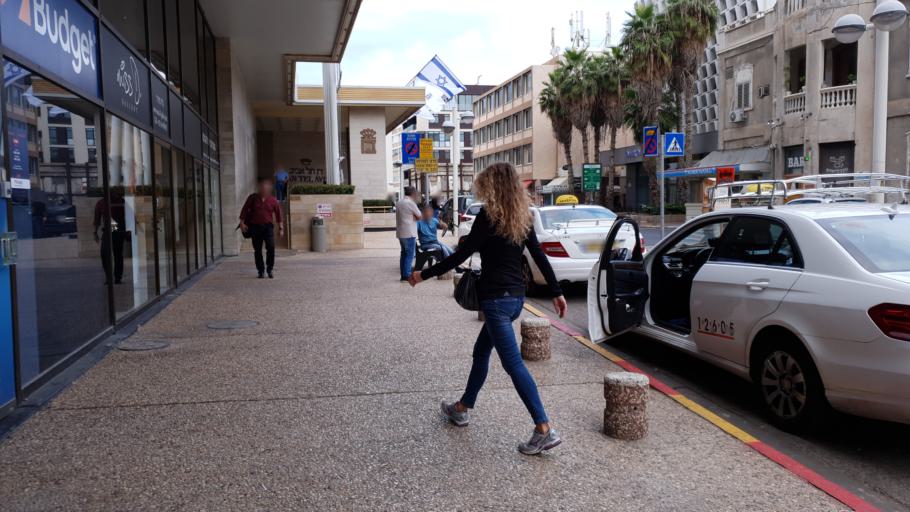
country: IL
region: Tel Aviv
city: Tel Aviv
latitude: 32.0792
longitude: 34.7678
